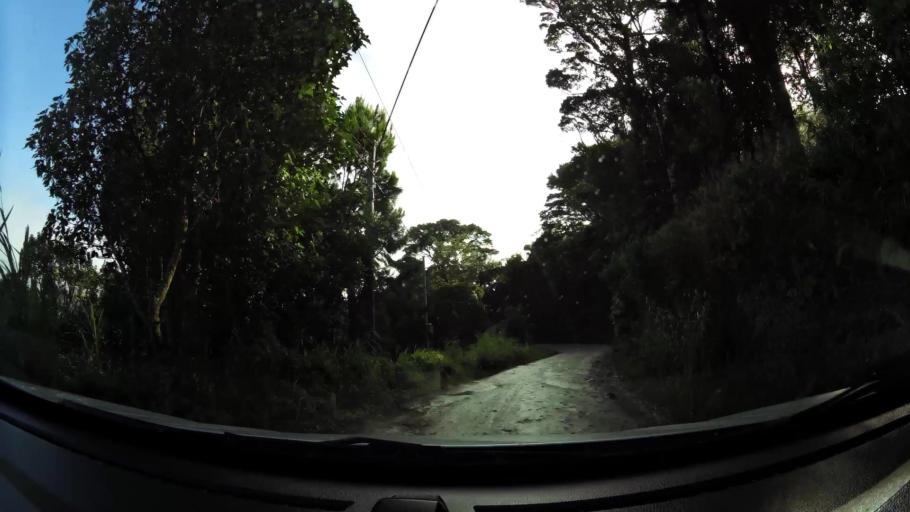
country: CR
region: Guanacaste
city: Juntas
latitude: 10.3015
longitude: -84.8037
